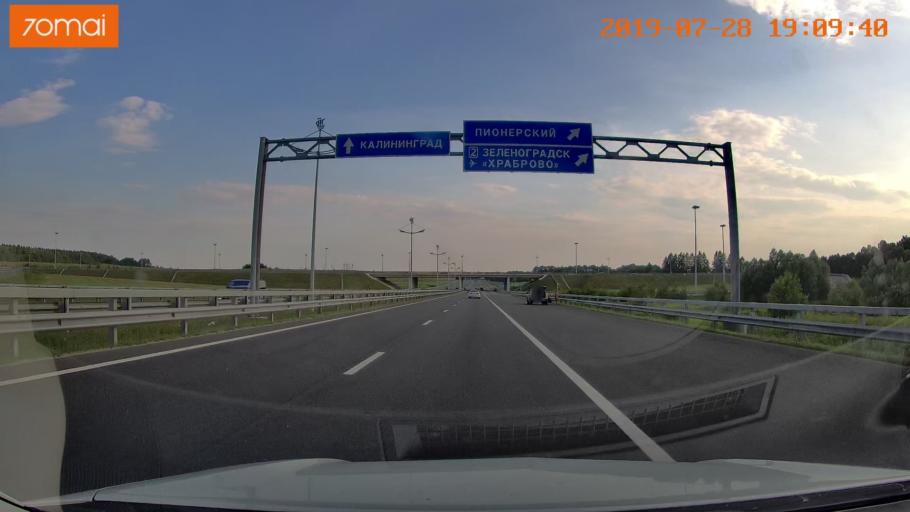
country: RU
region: Kaliningrad
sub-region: Gorod Kaliningrad
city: Pionerskiy
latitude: 54.9106
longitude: 20.1996
